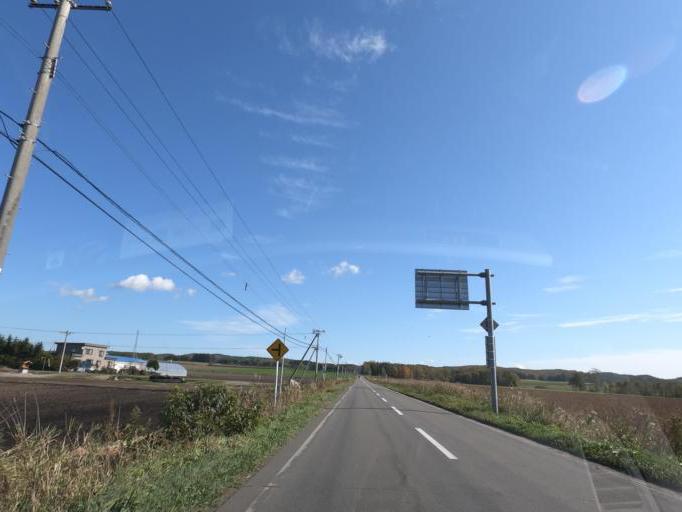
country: JP
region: Hokkaido
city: Otofuke
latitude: 43.0423
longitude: 143.2722
